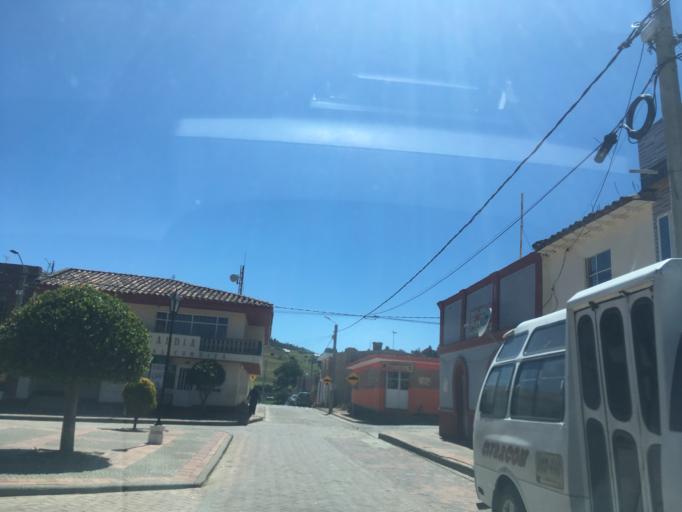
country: CO
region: Boyaca
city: Combita
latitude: 5.6335
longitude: -73.3247
